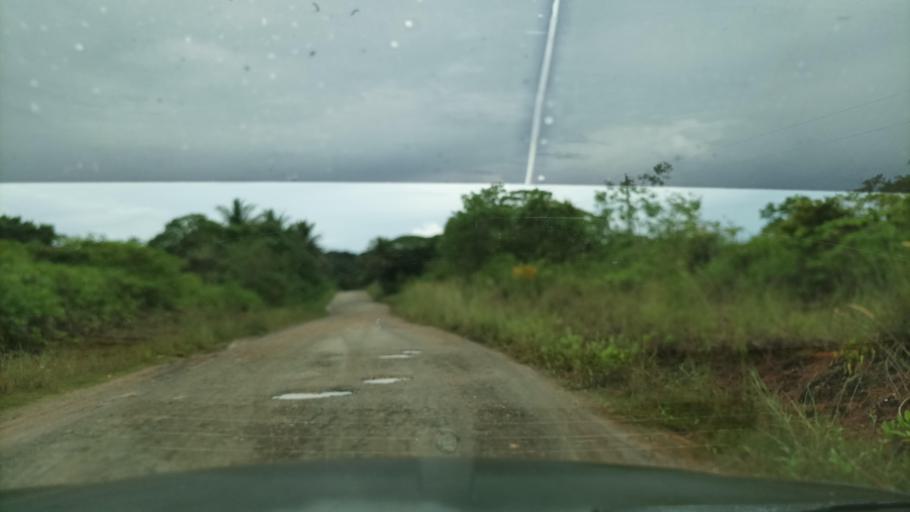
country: FM
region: Yap
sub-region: Weloy Municipality
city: Colonia
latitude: 9.5425
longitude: 138.1655
